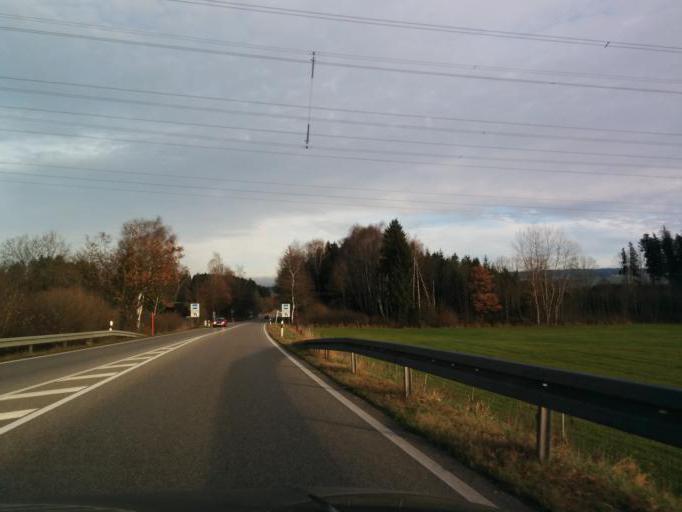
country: DE
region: Bavaria
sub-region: Swabia
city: Neuburg
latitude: 47.7437
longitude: 10.3572
